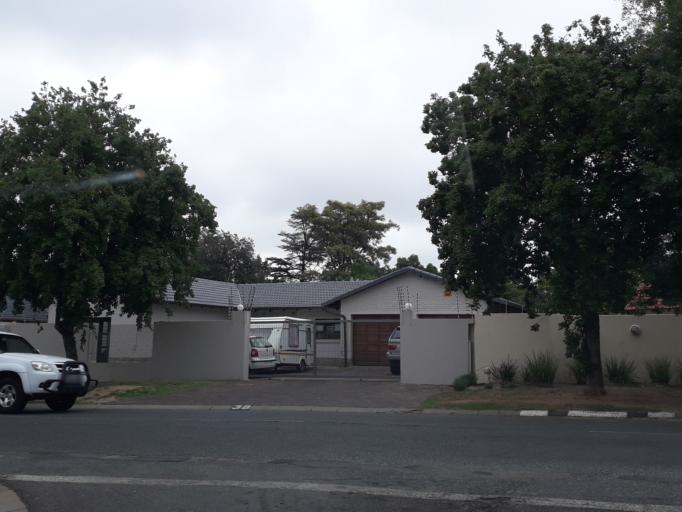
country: ZA
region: Gauteng
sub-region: City of Johannesburg Metropolitan Municipality
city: Roodepoort
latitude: -26.1099
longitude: 27.9454
